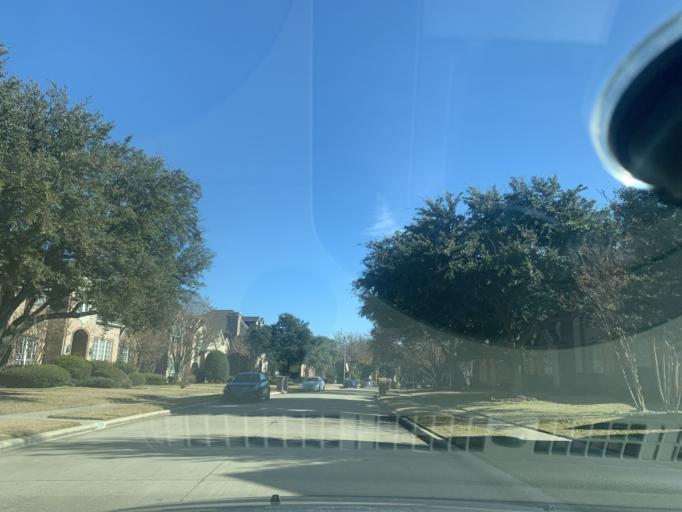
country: US
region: Texas
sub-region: Denton County
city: The Colony
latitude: 33.0518
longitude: -96.8196
